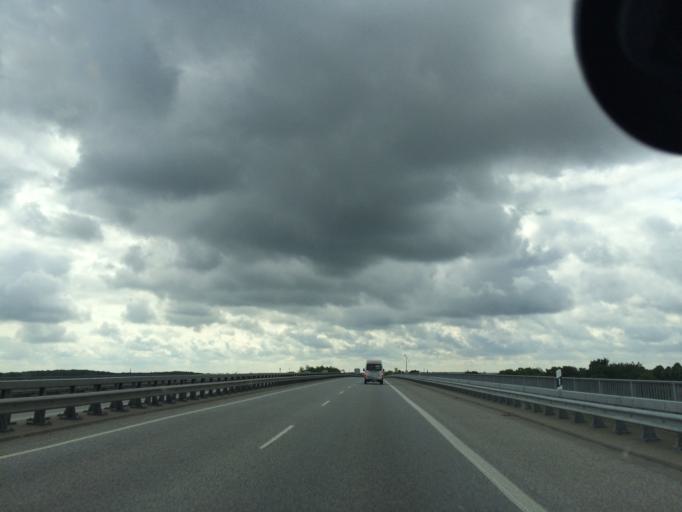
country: DE
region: Schleswig-Holstein
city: Ottendorf
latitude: 54.3691
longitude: 10.0760
